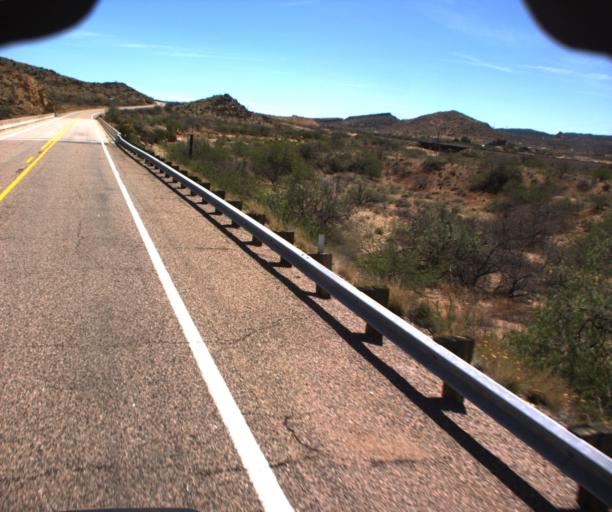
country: US
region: Arizona
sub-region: Mohave County
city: New Kingman-Butler
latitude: 35.3806
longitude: -113.7295
